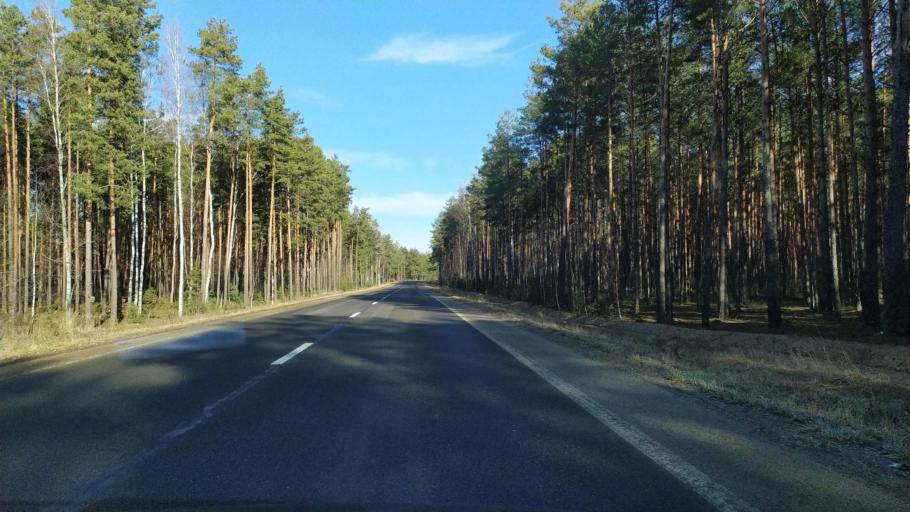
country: BY
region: Brest
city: Zhabinka
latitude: 52.4512
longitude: 24.1371
